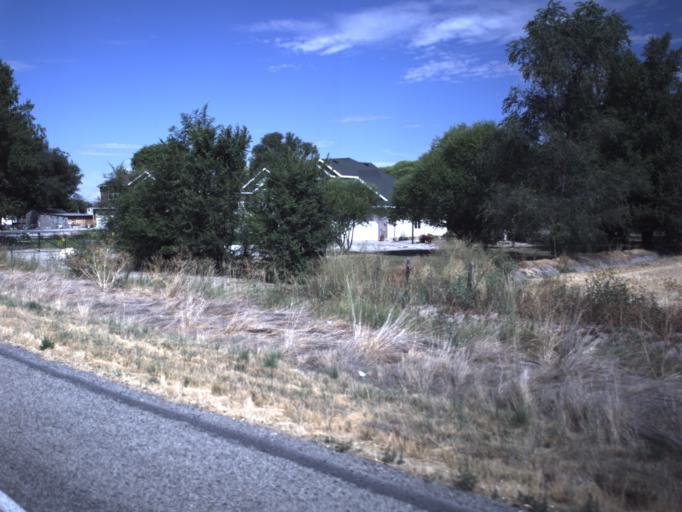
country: US
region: Utah
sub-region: Box Elder County
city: Brigham City
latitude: 41.5378
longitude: -112.0772
